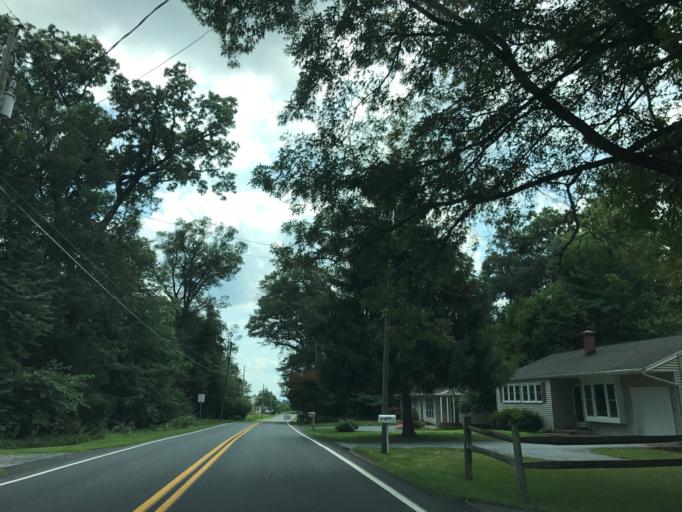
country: US
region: Pennsylvania
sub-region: Lancaster County
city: Manheim
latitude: 40.1887
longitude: -76.4571
